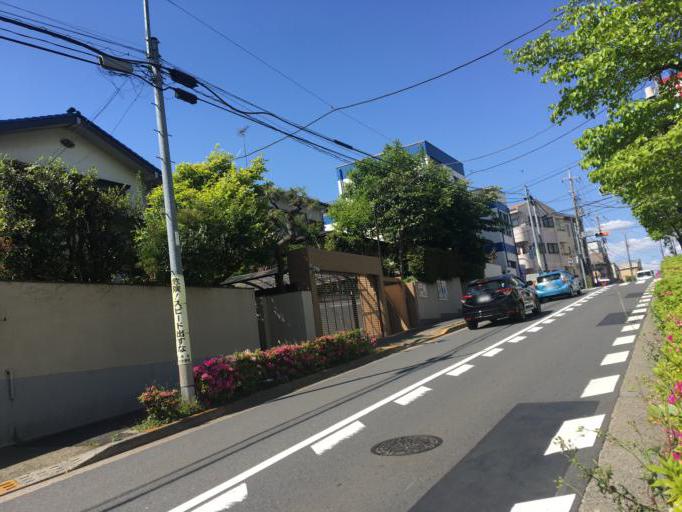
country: JP
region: Saitama
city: Wako
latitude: 35.7783
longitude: 139.6365
